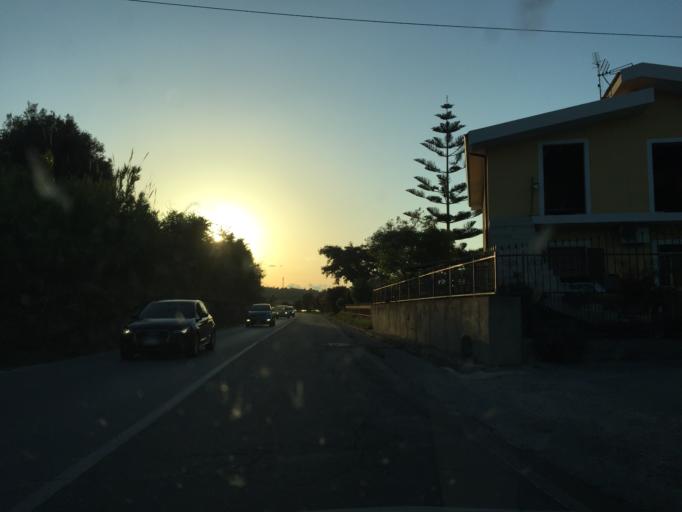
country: IT
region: Calabria
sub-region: Provincia di Vibo-Valentia
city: Pannaconi
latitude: 38.7161
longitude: 16.0566
